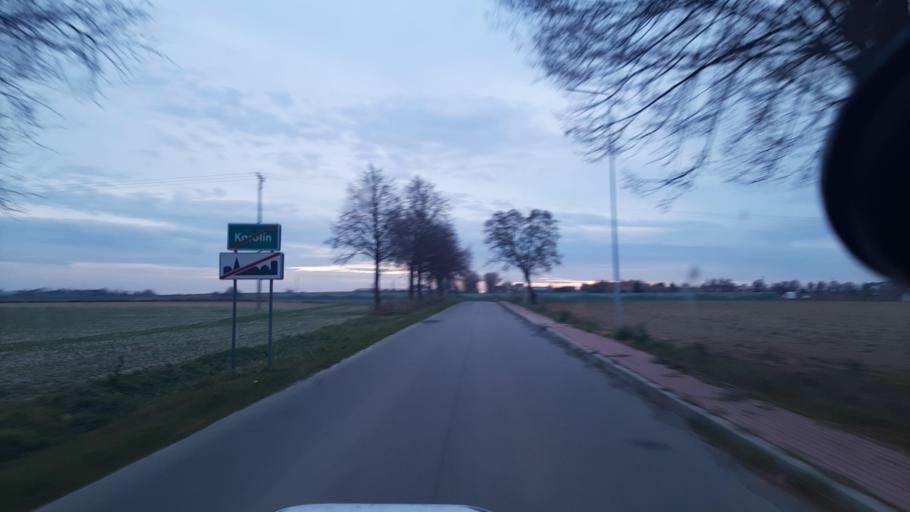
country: PL
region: Lublin Voivodeship
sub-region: Powiat lubelski
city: Garbow
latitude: 51.3537
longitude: 22.3692
